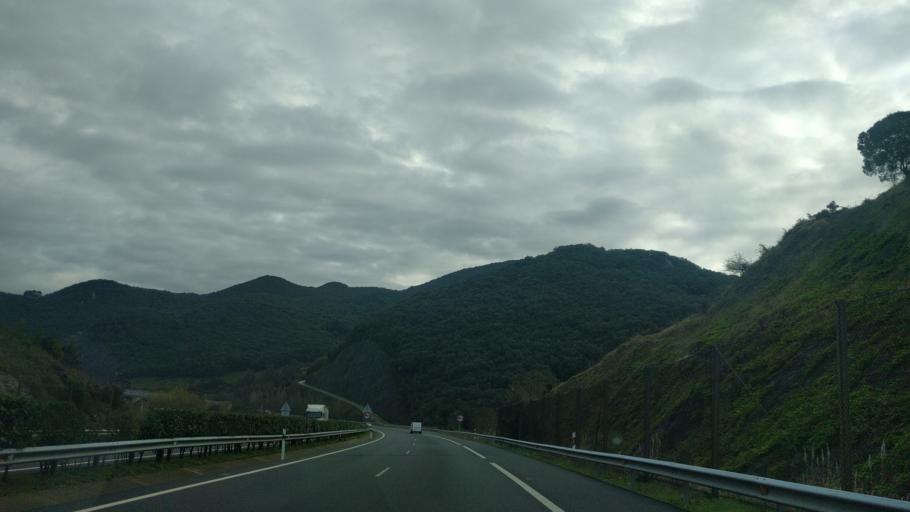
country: ES
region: Cantabria
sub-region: Provincia de Cantabria
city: Liendo
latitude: 43.3805
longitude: -3.3751
